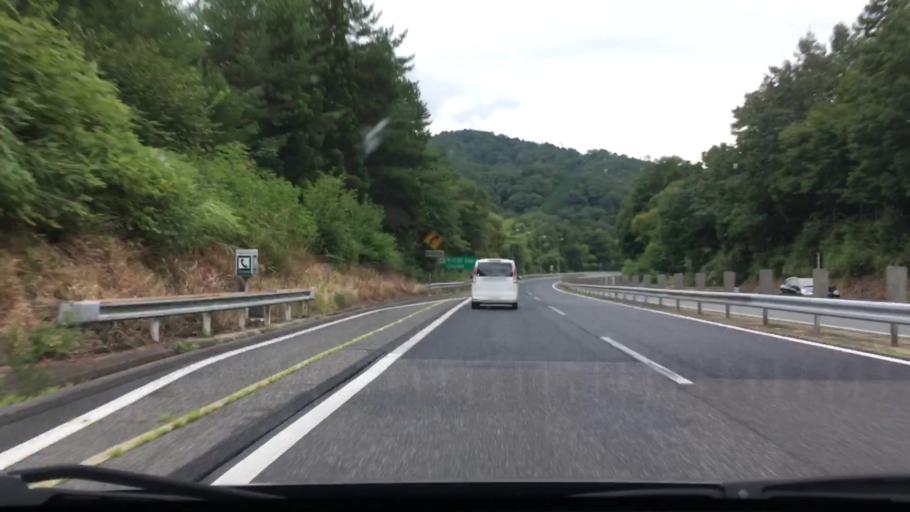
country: JP
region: Hiroshima
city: Hiroshima-shi
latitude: 34.6815
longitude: 132.5613
